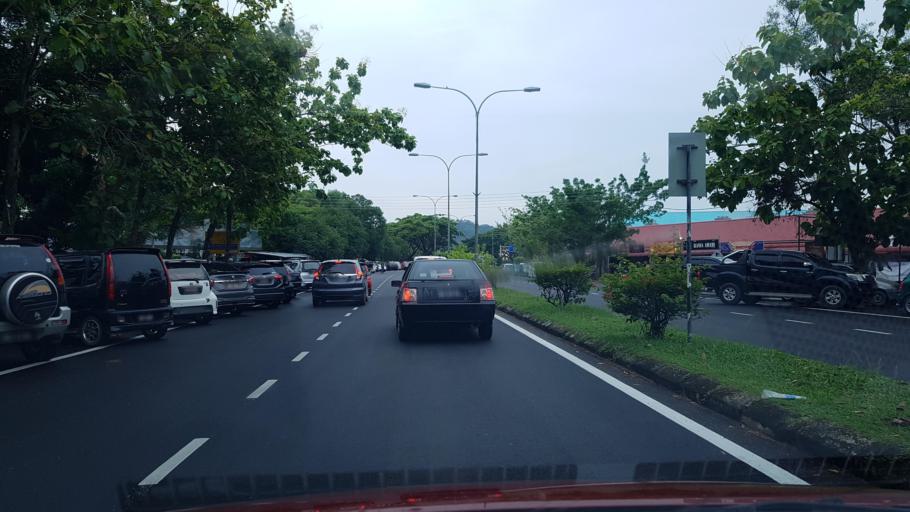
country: MY
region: Terengganu
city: Kuala Terengganu
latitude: 5.3119
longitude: 103.1282
